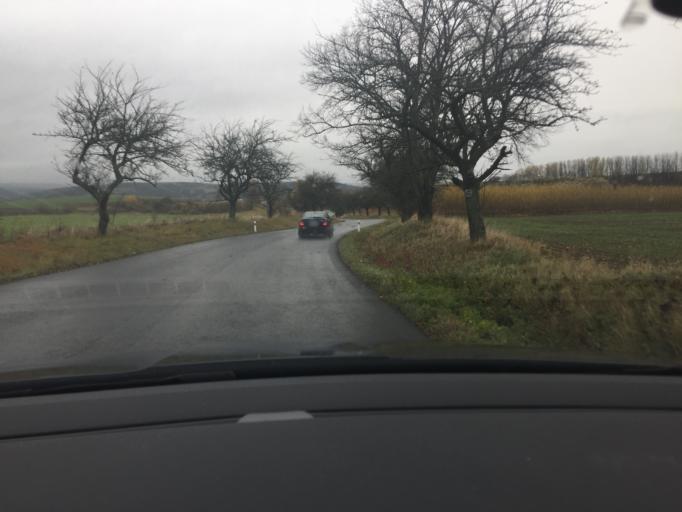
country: SK
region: Presovsky
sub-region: Okres Presov
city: Kezmarok
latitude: 49.1709
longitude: 20.4094
